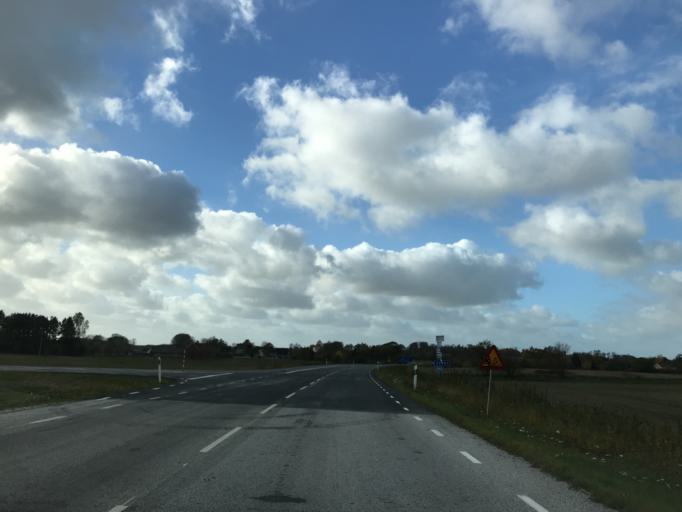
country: SE
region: Skane
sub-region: Bjuvs Kommun
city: Billesholm
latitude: 56.0103
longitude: 12.9646
